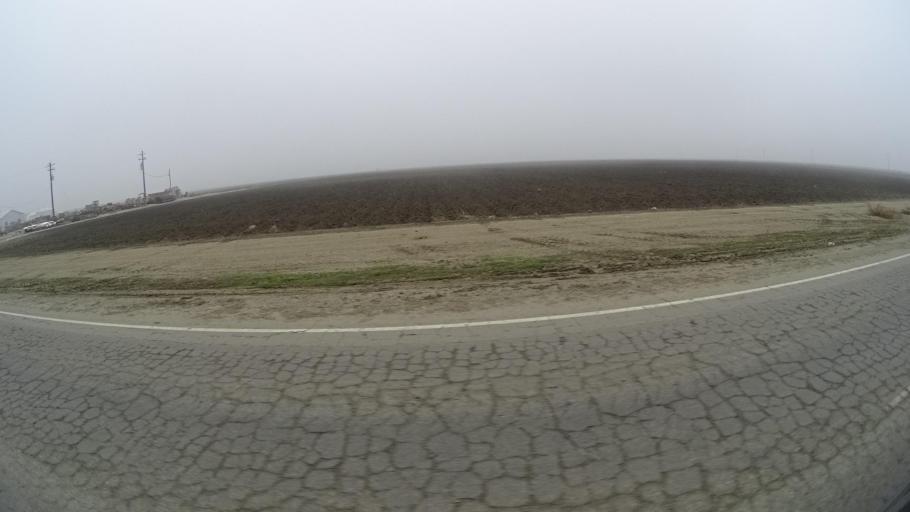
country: US
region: California
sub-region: Kern County
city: Buttonwillow
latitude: 35.4393
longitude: -119.5180
